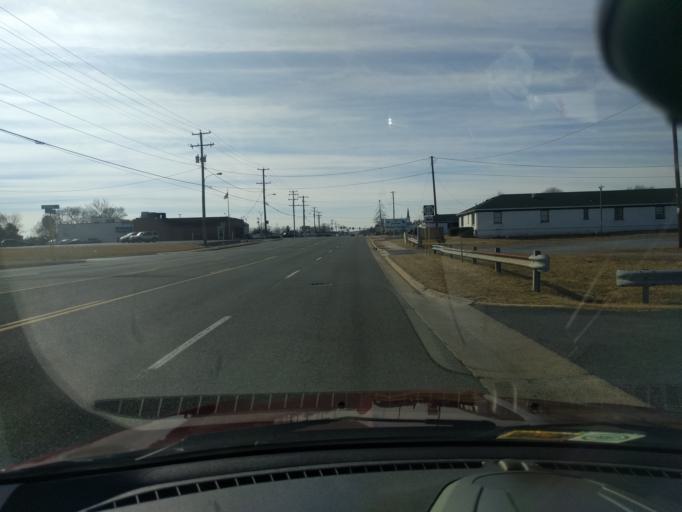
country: US
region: Virginia
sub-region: Augusta County
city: Verona
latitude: 38.2042
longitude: -79.0061
